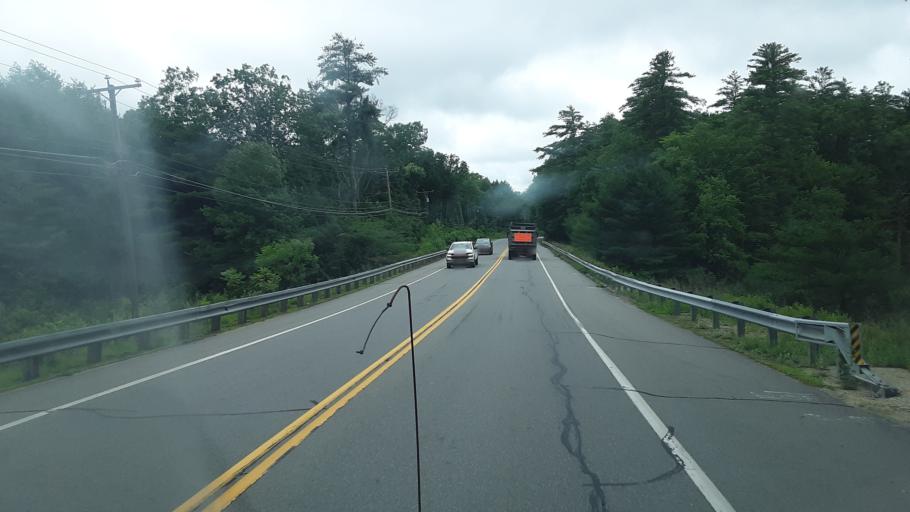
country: US
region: New Hampshire
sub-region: Rockingham County
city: Nottingham
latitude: 43.1576
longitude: -71.0687
